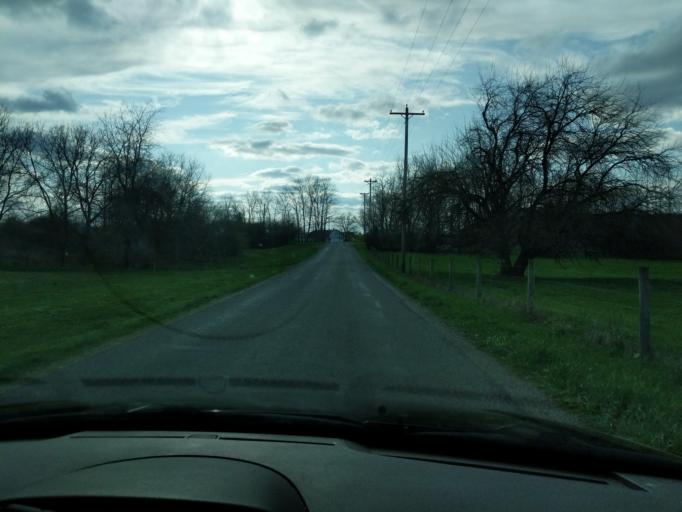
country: US
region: Ohio
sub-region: Champaign County
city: Urbana
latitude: 40.1448
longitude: -83.6992
